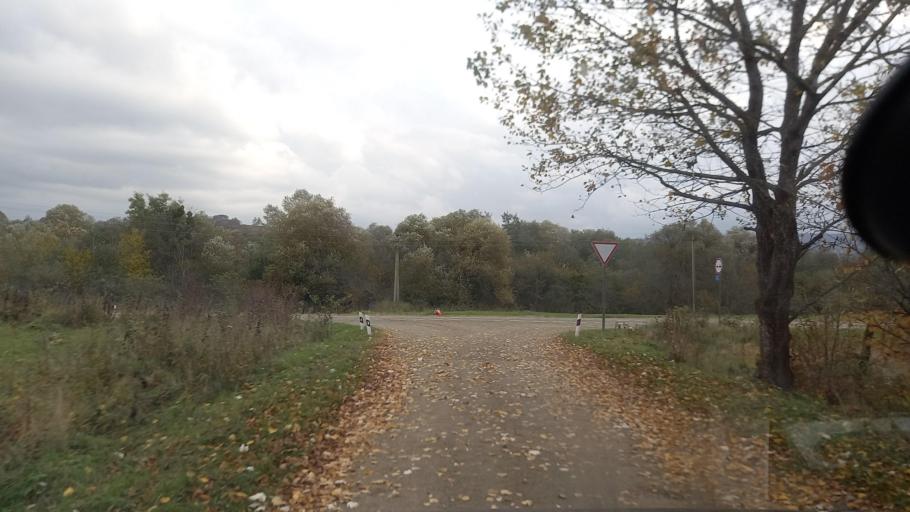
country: RU
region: Krasnodarskiy
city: Gubskaya
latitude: 44.3020
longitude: 40.5533
